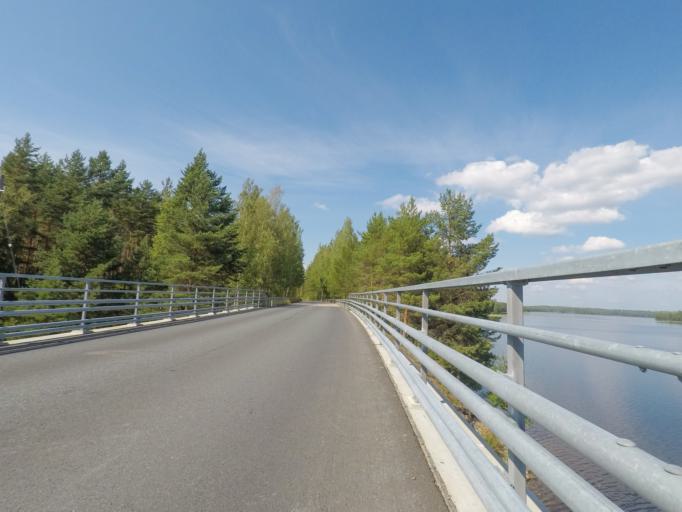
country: FI
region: Southern Savonia
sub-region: Mikkeli
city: Puumala
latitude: 61.4687
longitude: 28.1690
